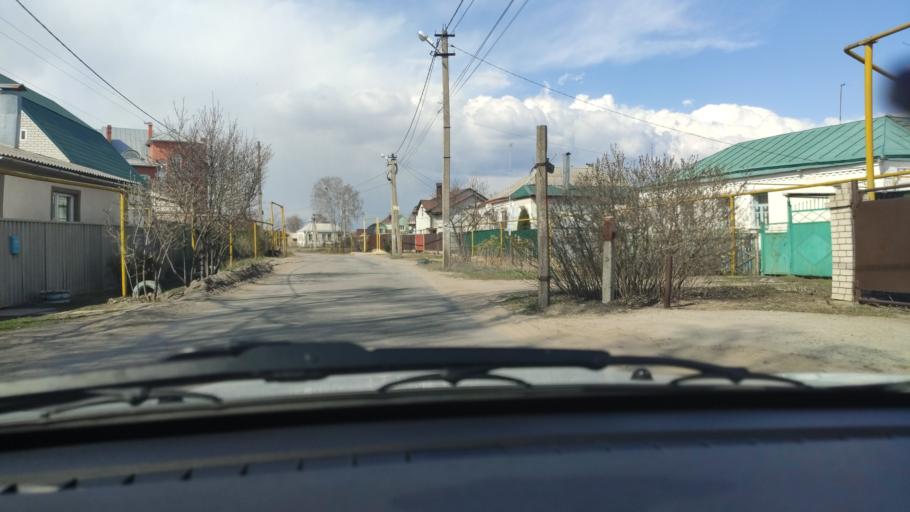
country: RU
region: Voronezj
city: Podgornoye
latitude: 51.7381
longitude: 39.1558
